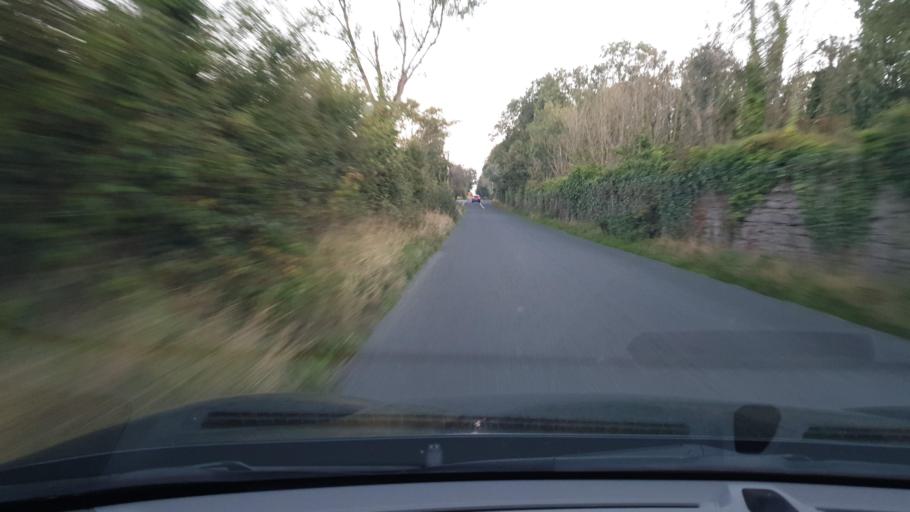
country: IE
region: Leinster
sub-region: Kildare
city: Prosperous
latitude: 53.3482
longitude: -6.7471
